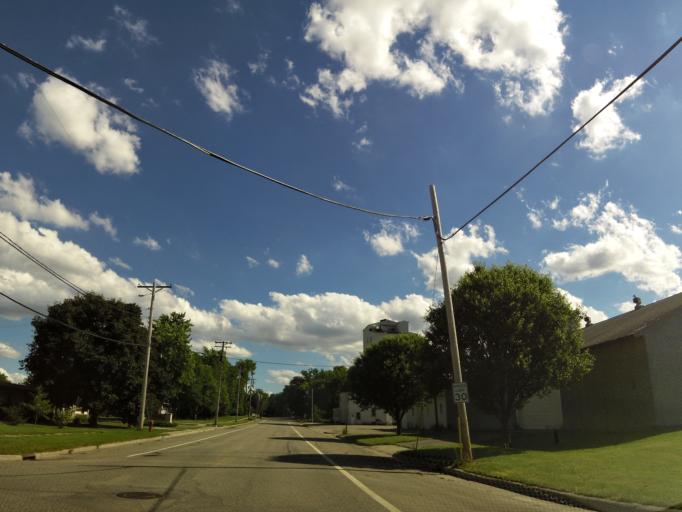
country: US
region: Minnesota
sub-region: Meeker County
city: Dassel
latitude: 45.0861
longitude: -94.3074
